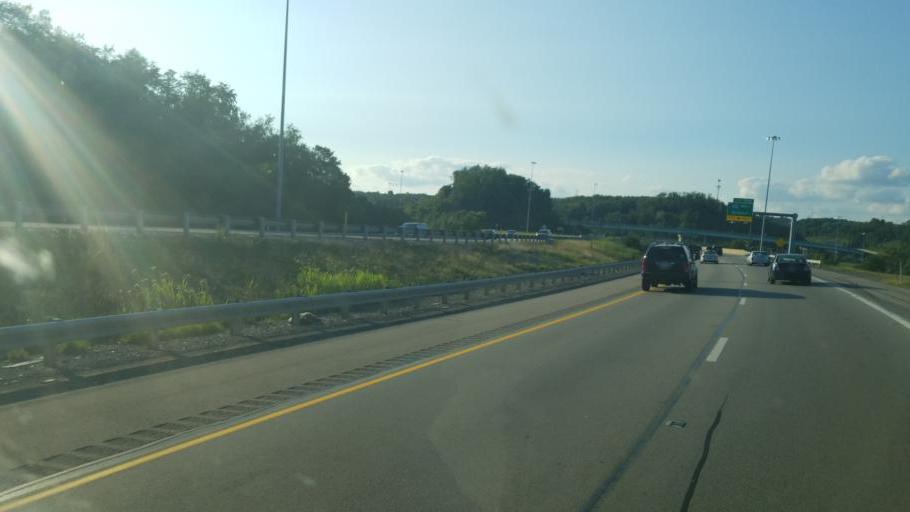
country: US
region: Pennsylvania
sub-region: Allegheny County
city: Carnegie
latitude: 40.4195
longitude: -80.1032
